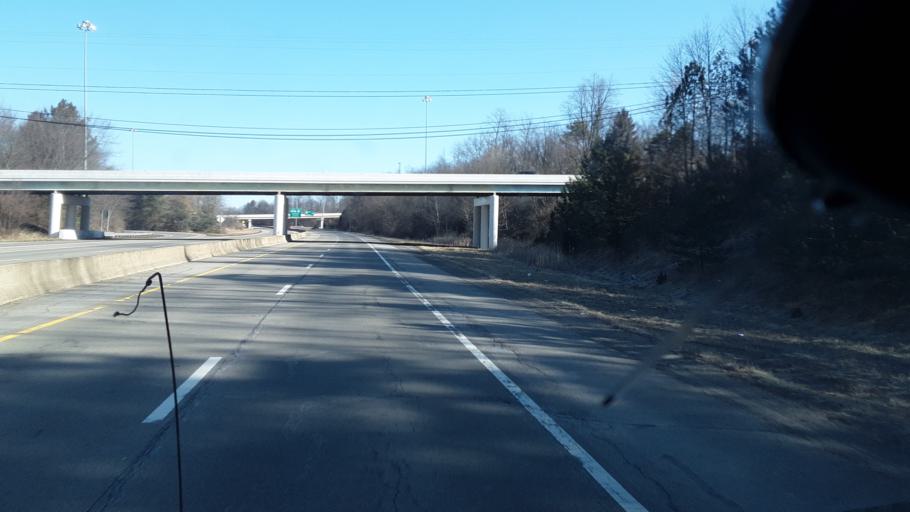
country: US
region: Ohio
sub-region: Wayne County
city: Wooster
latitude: 40.7923
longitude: -81.9138
